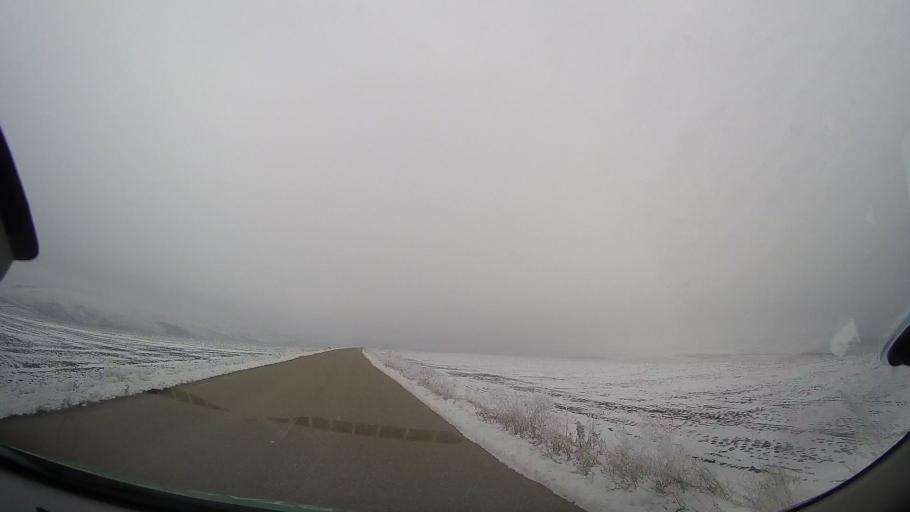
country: RO
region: Vaslui
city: Coroiesti
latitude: 46.2182
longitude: 27.4797
